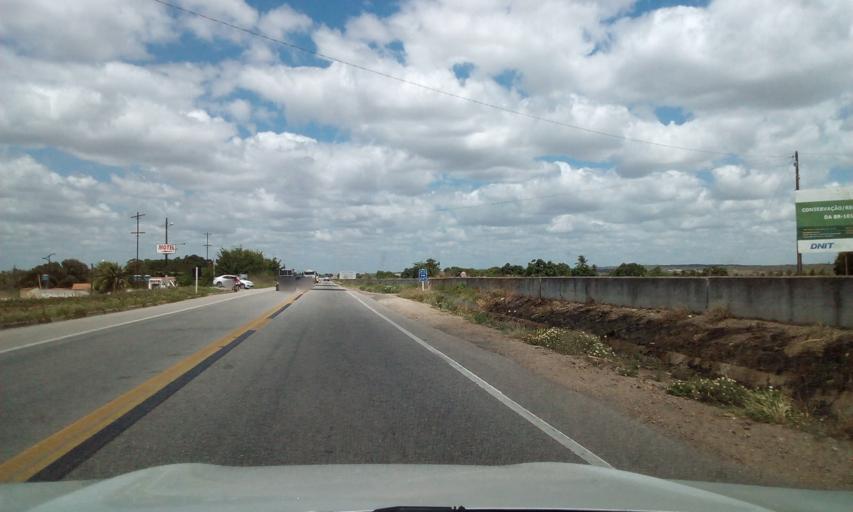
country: BR
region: Sergipe
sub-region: Propria
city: Propria
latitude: -10.1988
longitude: -36.8209
